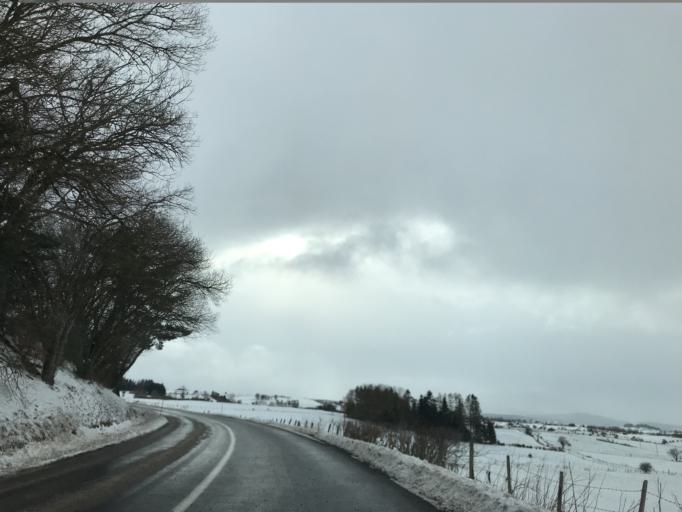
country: FR
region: Auvergne
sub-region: Departement du Puy-de-Dome
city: Aydat
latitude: 45.6832
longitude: 2.9372
